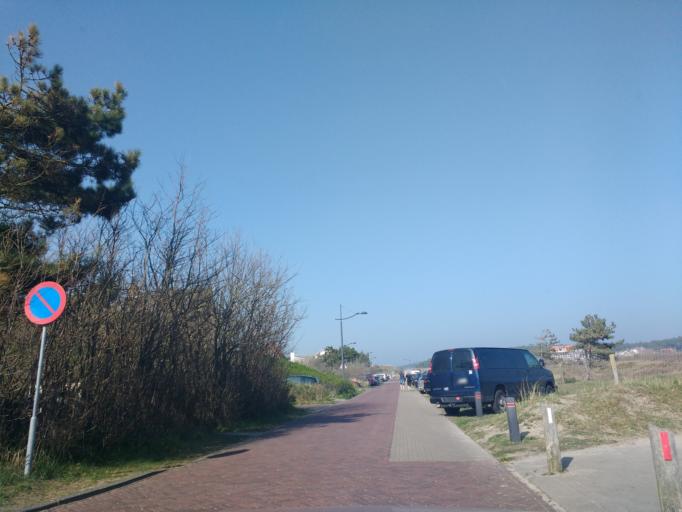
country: NL
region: North Holland
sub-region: Gemeente Bergen
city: Egmond aan Zee
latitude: 52.6636
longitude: 4.6317
